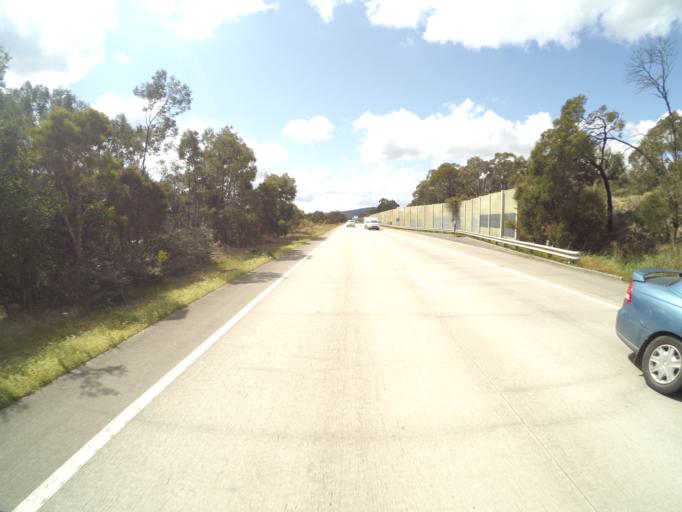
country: AU
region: New South Wales
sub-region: Wingecarribee
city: Mittagong
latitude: -34.4386
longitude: 150.4195
